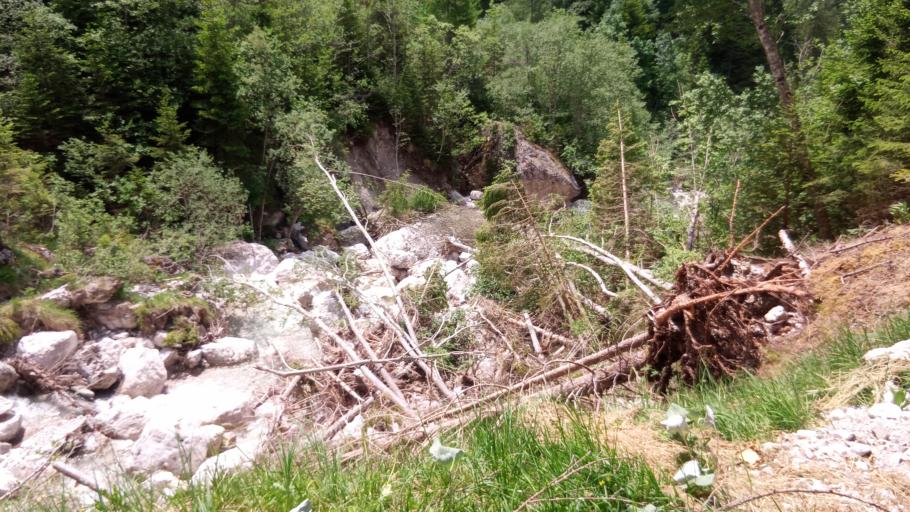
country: IT
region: Veneto
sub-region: Provincia di Belluno
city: La Valle Agordina
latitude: 46.2960
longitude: 12.0947
